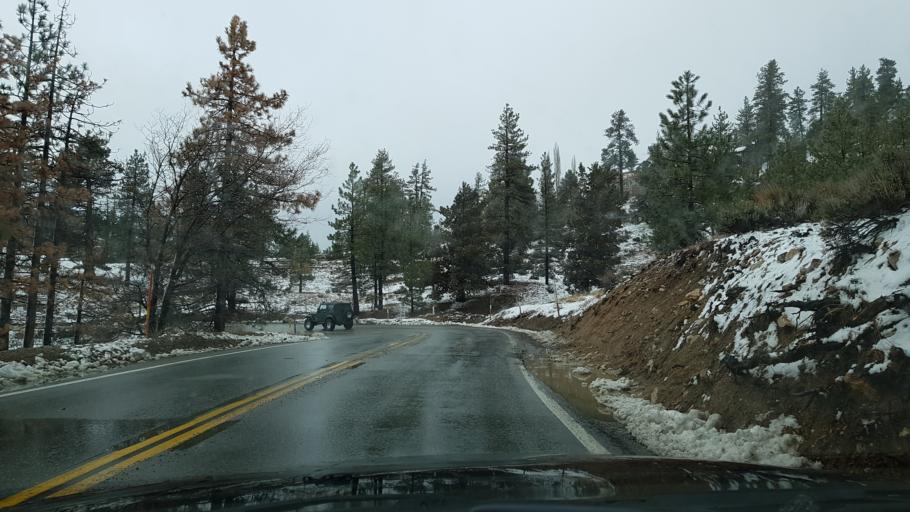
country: US
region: California
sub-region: San Bernardino County
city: Big Bear Lake
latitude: 34.2639
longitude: -116.9343
